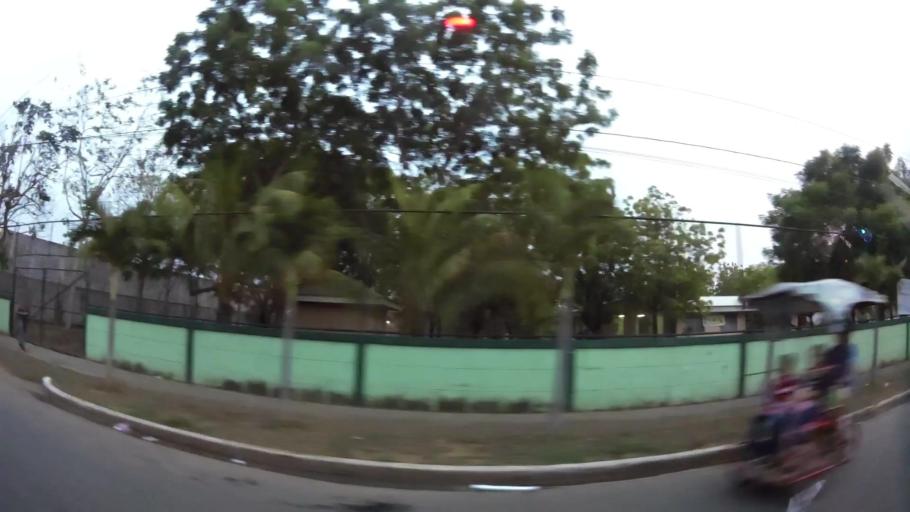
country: NI
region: Masaya
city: Nindiri
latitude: 12.0035
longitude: -86.1163
